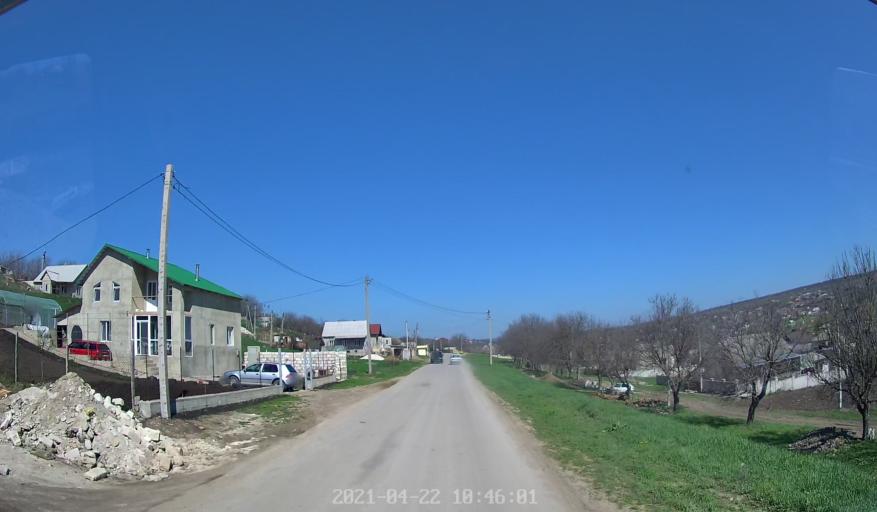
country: MD
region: Chisinau
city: Ciorescu
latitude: 47.1600
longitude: 28.9542
